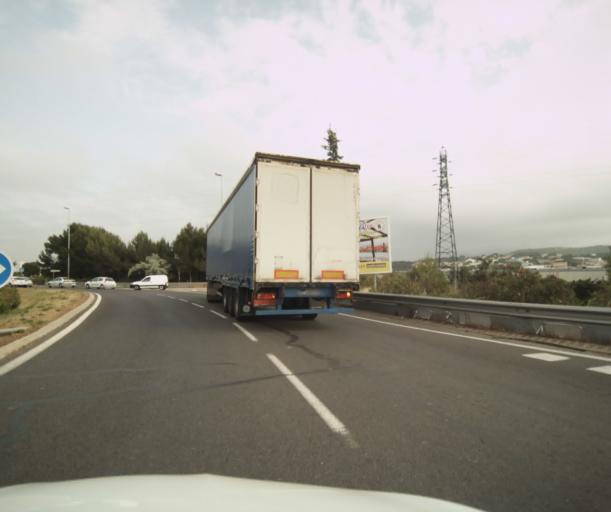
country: FR
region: Provence-Alpes-Cote d'Azur
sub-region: Departement du Var
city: Ollioules
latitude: 43.1195
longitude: 5.8521
